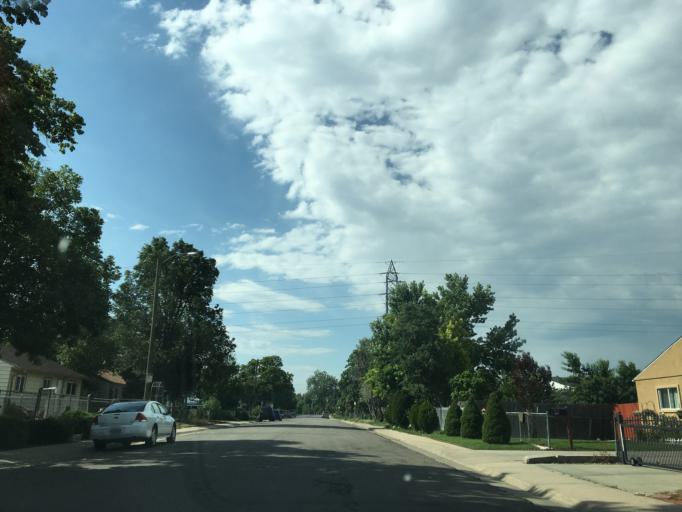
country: US
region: Colorado
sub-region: Jefferson County
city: Lakewood
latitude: 39.6996
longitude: -105.0357
